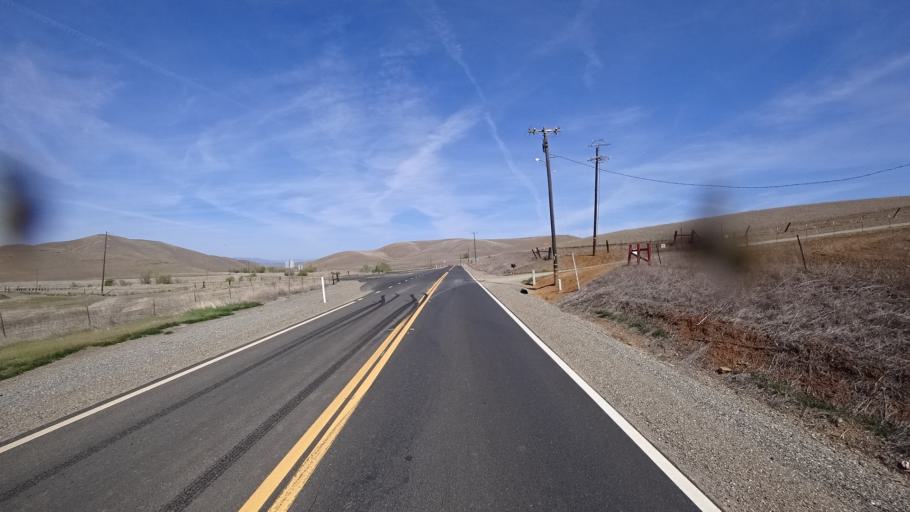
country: US
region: California
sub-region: Glenn County
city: Willows
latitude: 39.5528
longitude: -122.3574
